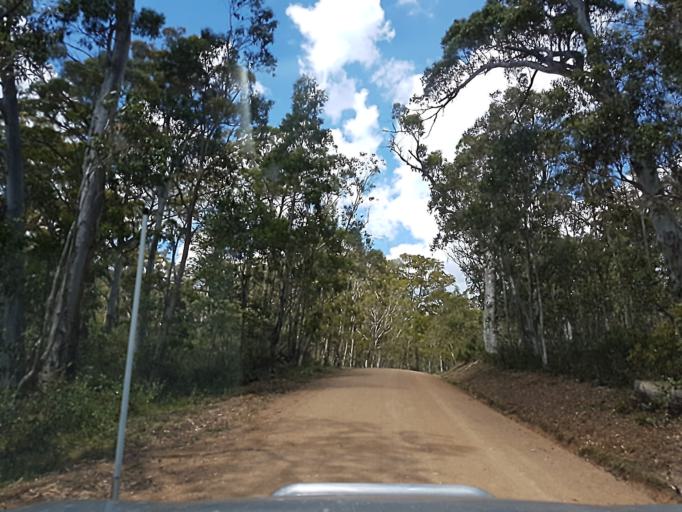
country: AU
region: New South Wales
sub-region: Snowy River
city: Jindabyne
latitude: -36.9032
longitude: 148.1028
